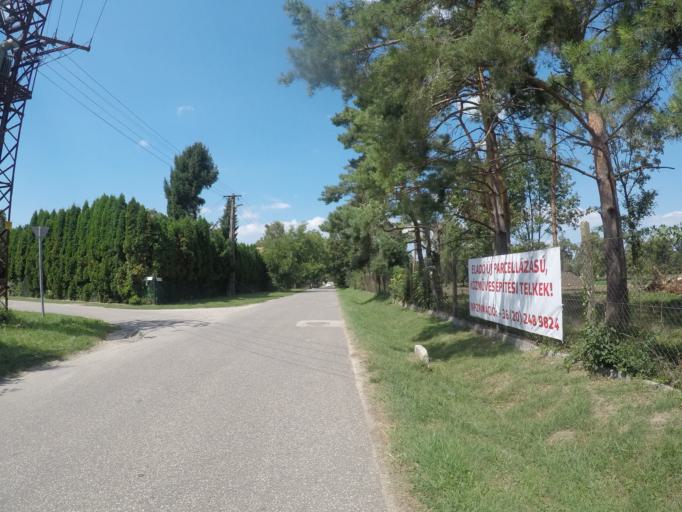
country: HU
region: Somogy
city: Balatonszabadi
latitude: 46.9299
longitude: 18.1261
